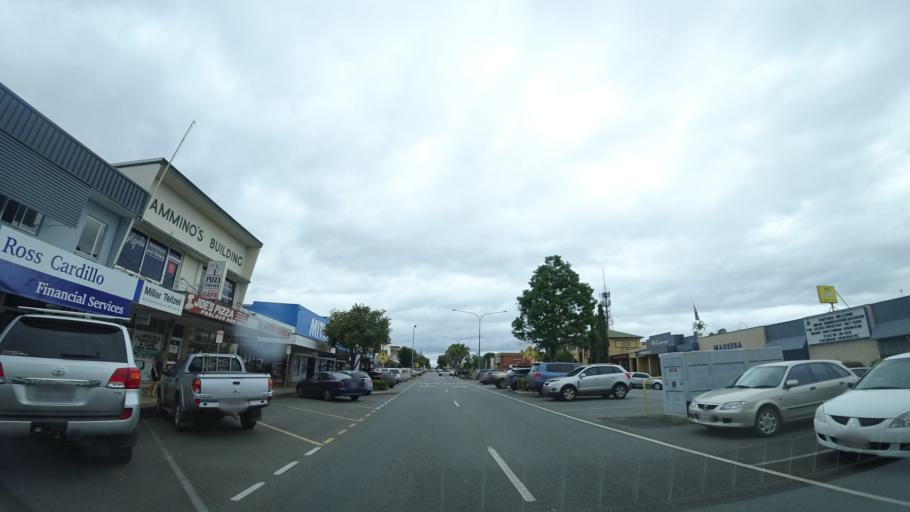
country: AU
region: Queensland
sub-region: Tablelands
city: Mareeba
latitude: -16.9913
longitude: 145.4222
